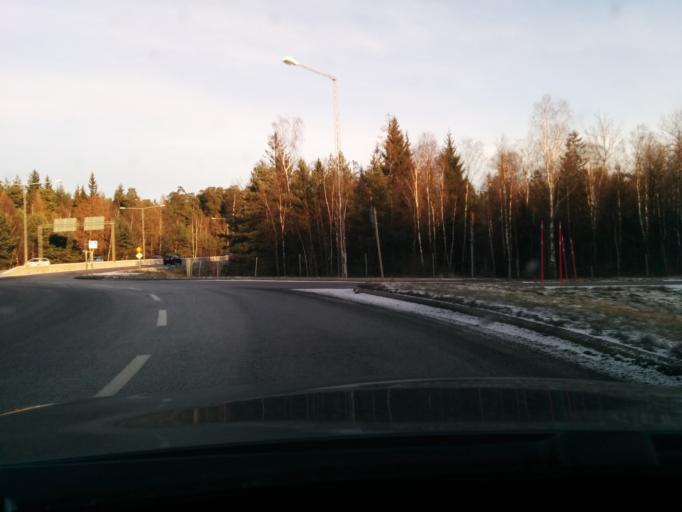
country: SE
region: Stockholm
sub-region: Jarfalla Kommun
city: Jakobsberg
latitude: 59.4729
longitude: 17.8123
